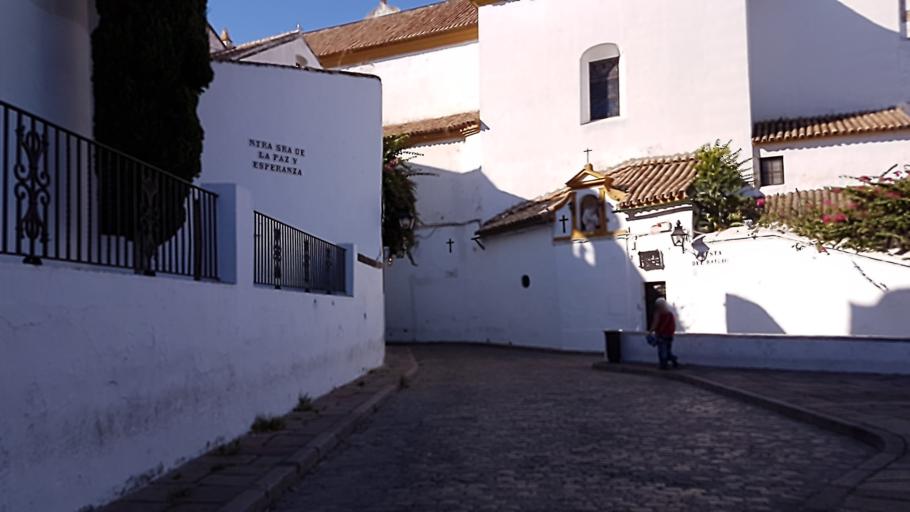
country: ES
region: Andalusia
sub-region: Province of Cordoba
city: Cordoba
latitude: 37.8874
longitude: -4.7767
